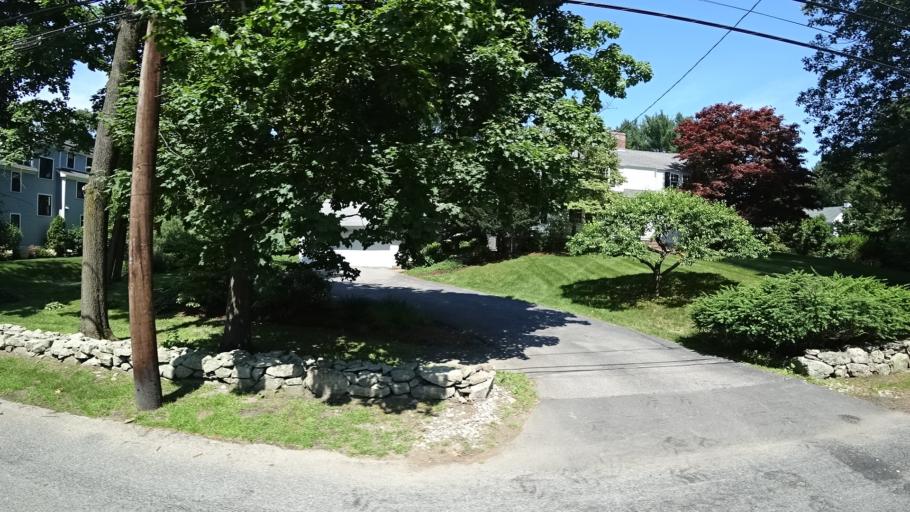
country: US
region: Massachusetts
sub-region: Norfolk County
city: Dedham
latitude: 42.2475
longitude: -71.1869
